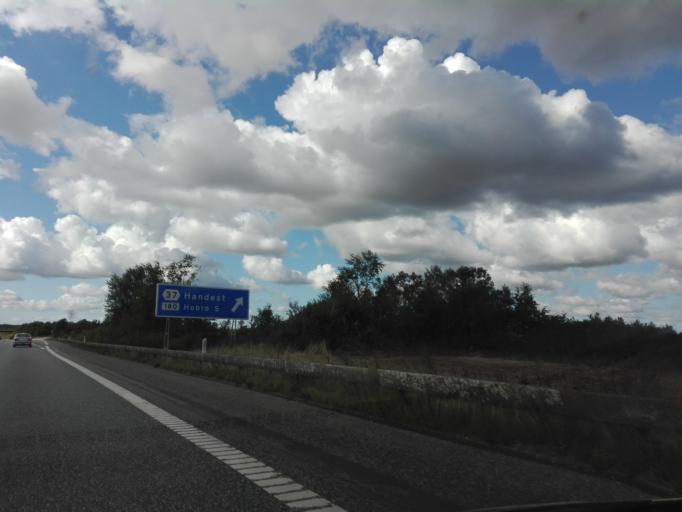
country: DK
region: North Denmark
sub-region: Mariagerfjord Kommune
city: Hobro
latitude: 56.5794
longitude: 9.8199
